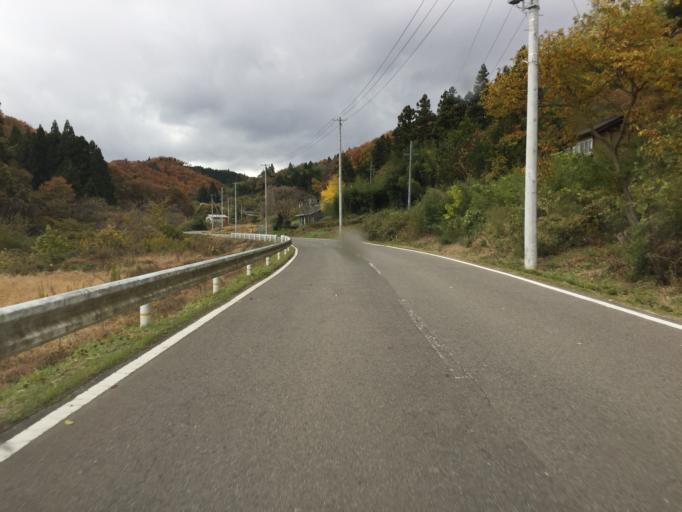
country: JP
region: Fukushima
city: Fukushima-shi
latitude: 37.7380
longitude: 140.5421
